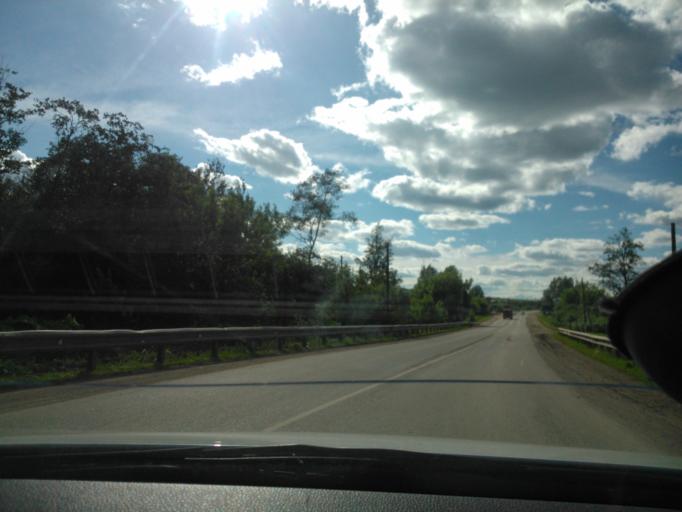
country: RU
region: Perm
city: Ust'-Kachka
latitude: 57.9418
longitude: 55.7483
